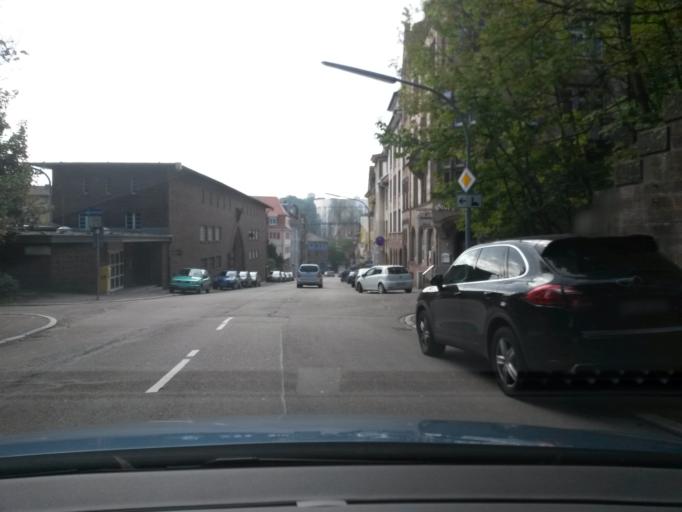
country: DE
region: Baden-Wuerttemberg
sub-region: Karlsruhe Region
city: Pforzheim
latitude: 48.8982
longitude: 8.7200
